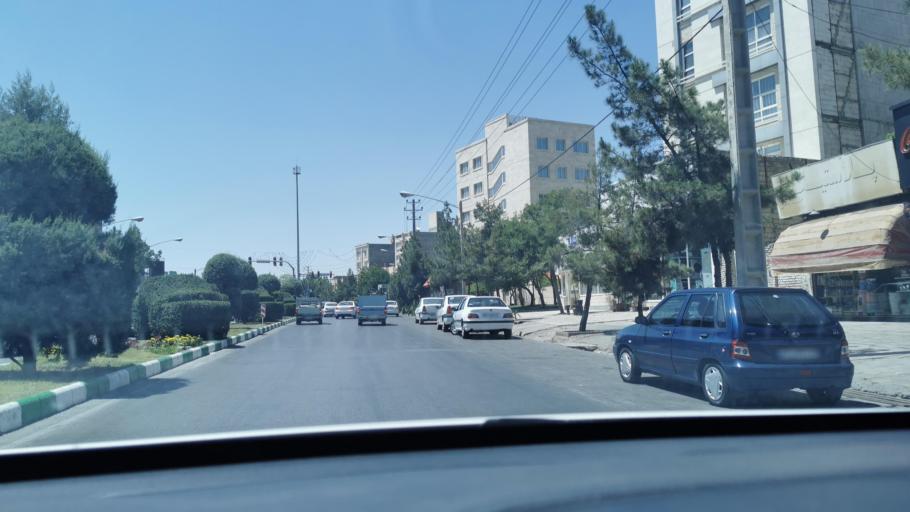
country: IR
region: Razavi Khorasan
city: Mashhad
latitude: 36.3398
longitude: 59.4844
